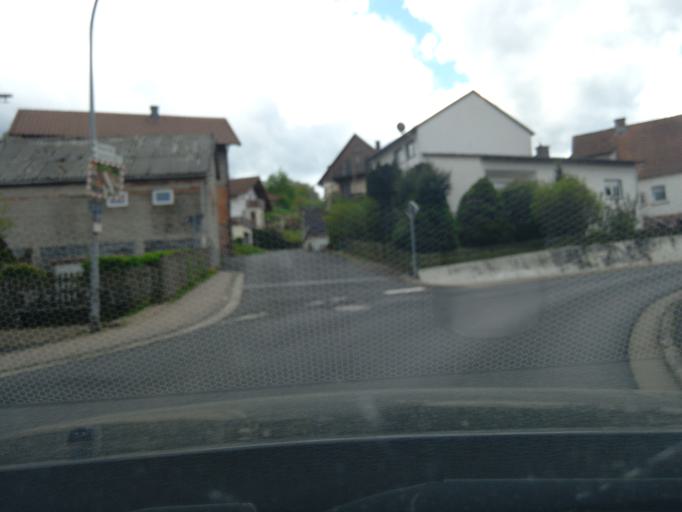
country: DE
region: Bavaria
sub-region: Regierungsbezirk Unterfranken
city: Aura im Sinngrund
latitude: 50.1684
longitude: 9.4750
